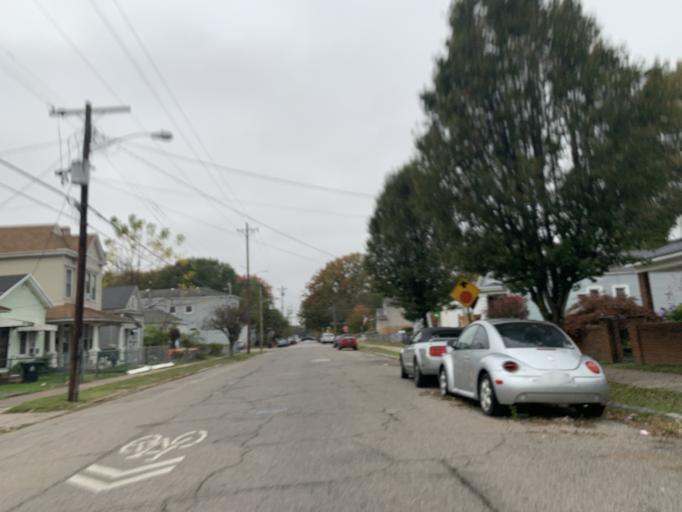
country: US
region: Kentucky
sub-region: Jefferson County
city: Louisville
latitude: 38.2616
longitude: -85.7885
